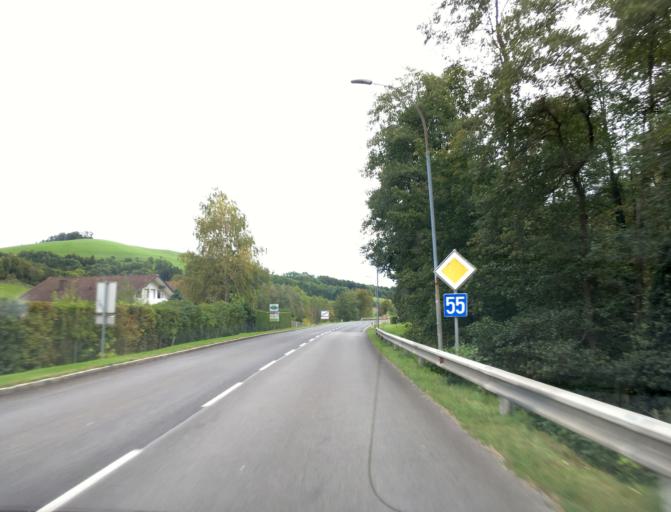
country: AT
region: Lower Austria
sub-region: Politischer Bezirk Wiener Neustadt
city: Bad Schonau
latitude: 47.5173
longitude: 16.1949
